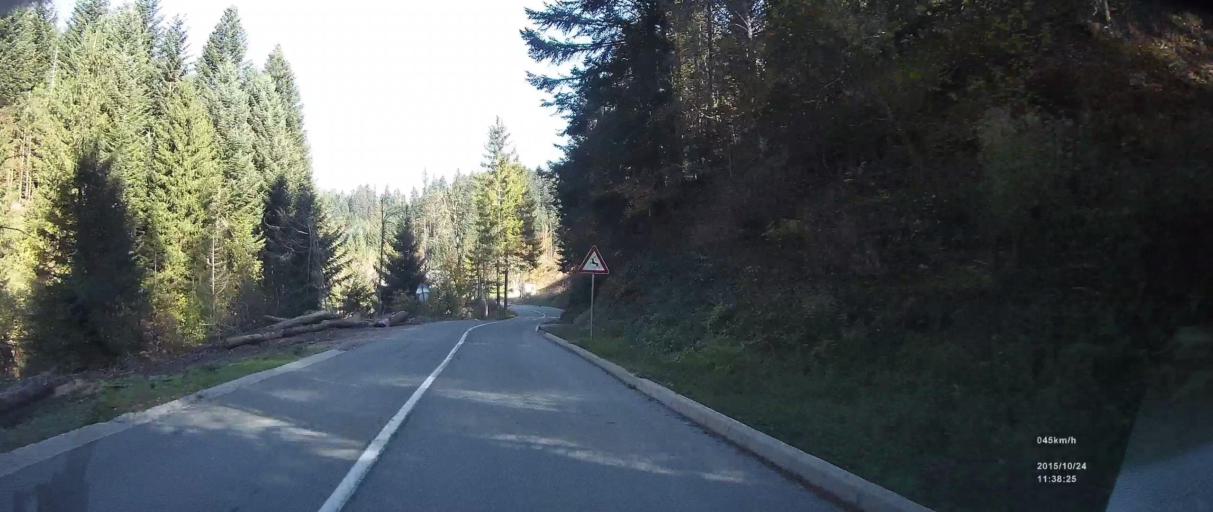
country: HR
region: Primorsko-Goranska
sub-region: Grad Delnice
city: Delnice
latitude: 45.4039
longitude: 14.7003
